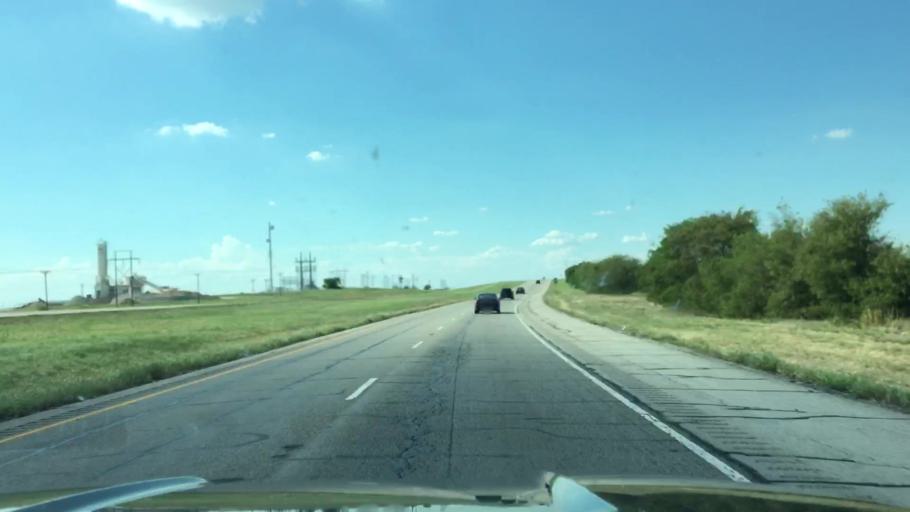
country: US
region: Texas
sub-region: Wise County
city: Decatur
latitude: 33.1755
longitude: -97.5430
